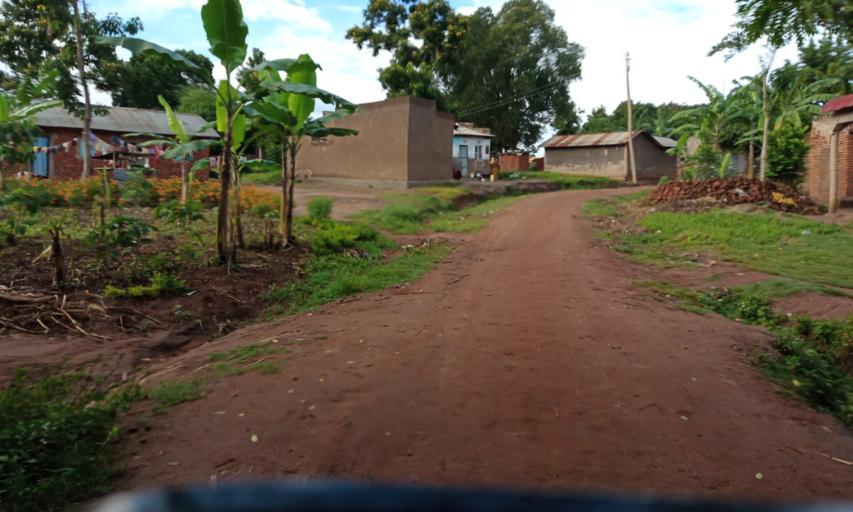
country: UG
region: Eastern Region
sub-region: Mbale District
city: Mbale
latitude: 1.1472
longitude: 34.1668
